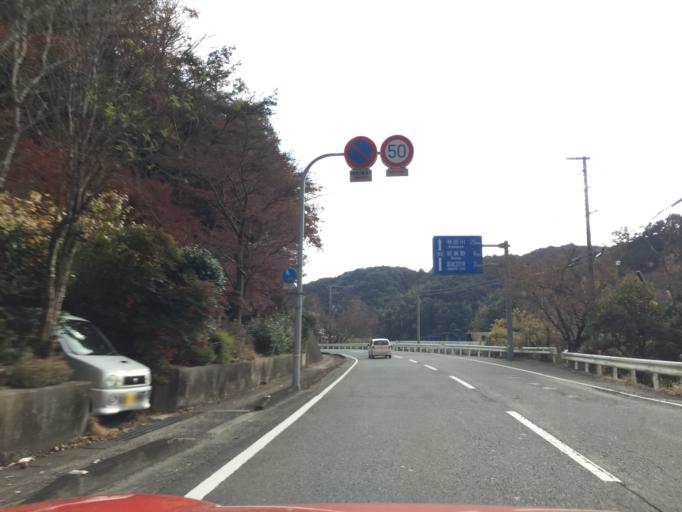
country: JP
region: Wakayama
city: Kainan
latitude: 34.1648
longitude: 135.2525
